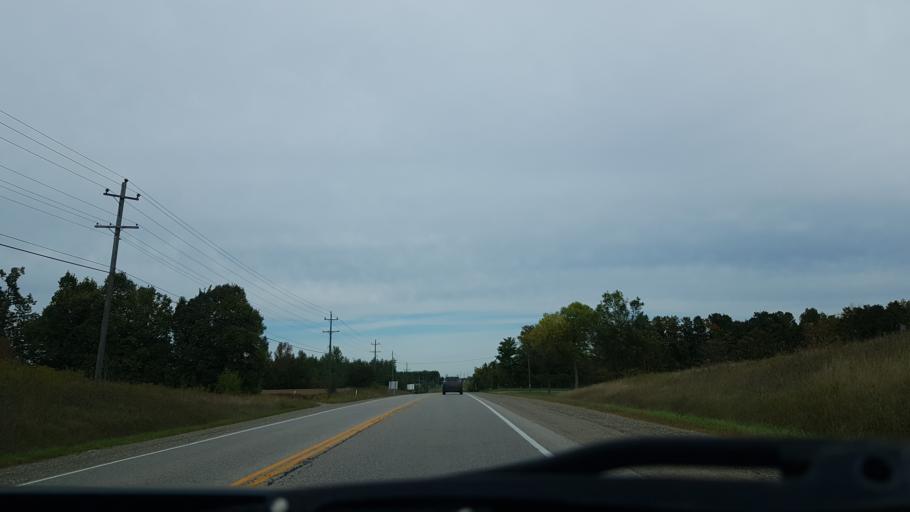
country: CA
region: Ontario
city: Orangeville
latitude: 43.7980
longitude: -80.0643
